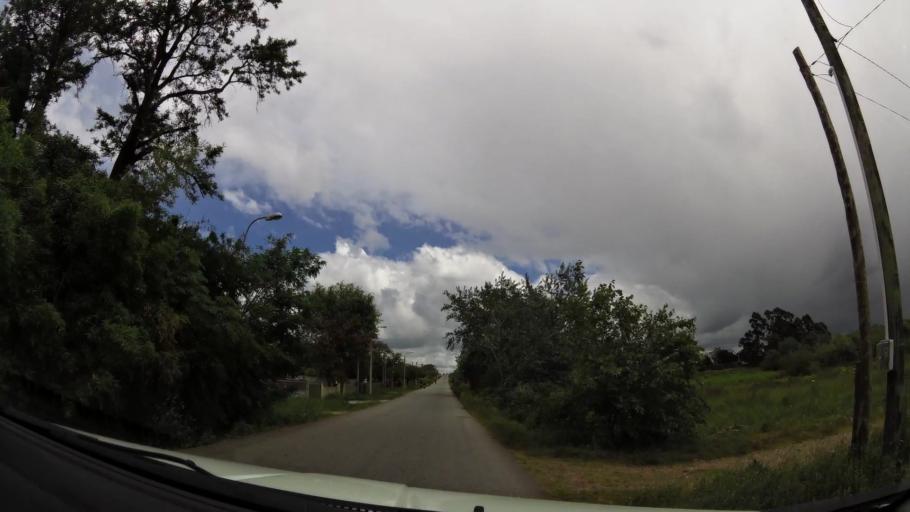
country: UY
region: Canelones
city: La Paz
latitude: -34.8029
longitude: -56.1593
